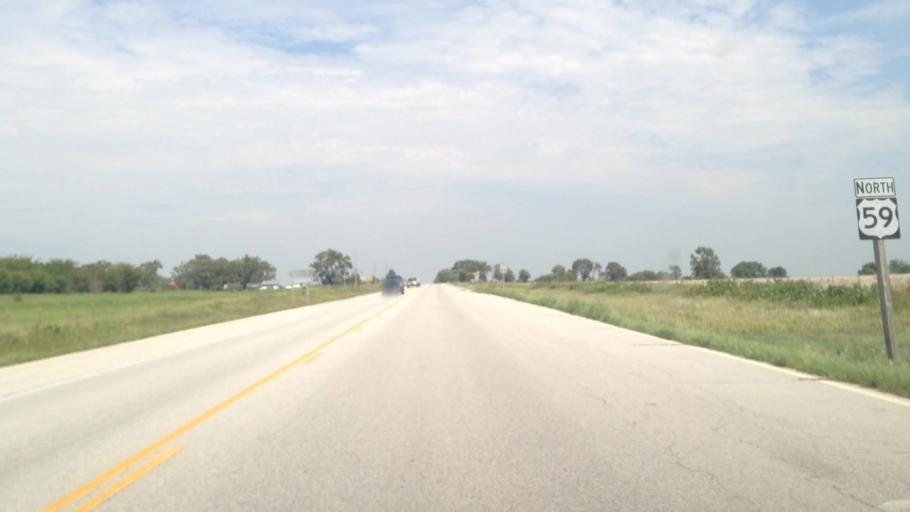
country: US
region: Kansas
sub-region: Neosho County
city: Erie
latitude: 37.4715
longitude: -95.2693
